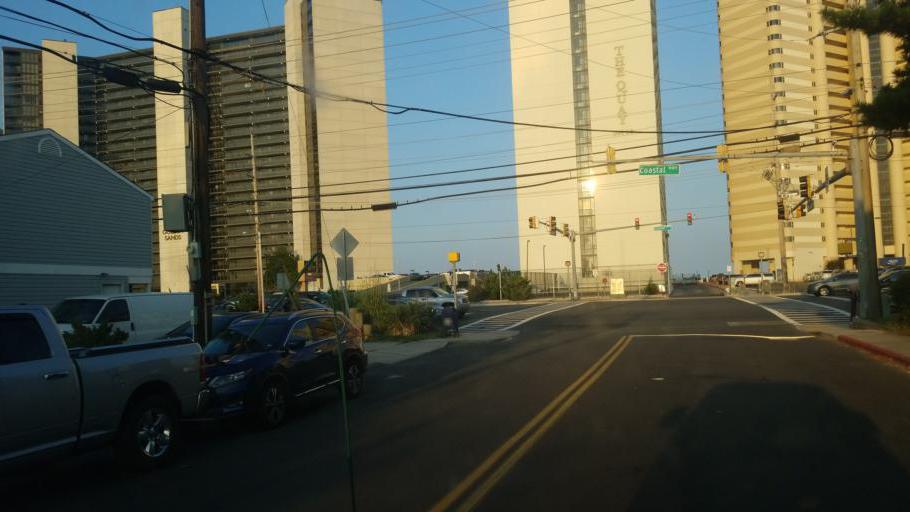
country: US
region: Maryland
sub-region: Worcester County
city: Ocean City
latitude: 38.4156
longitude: -75.0581
